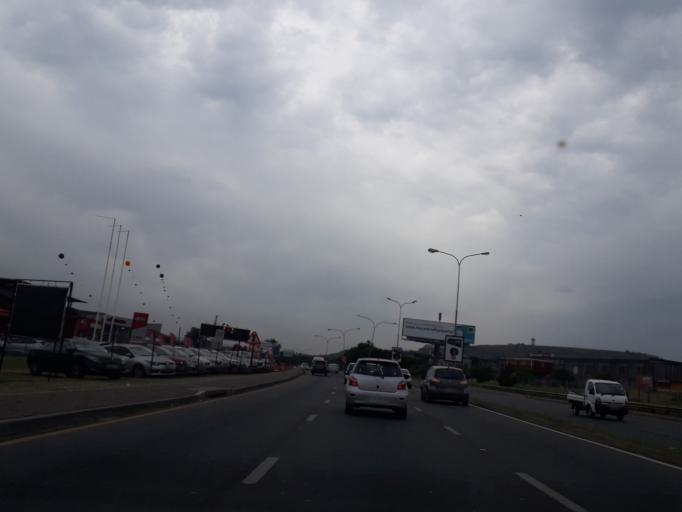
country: ZA
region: Gauteng
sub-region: City of Johannesburg Metropolitan Municipality
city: Roodepoort
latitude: -26.1174
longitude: 27.9556
